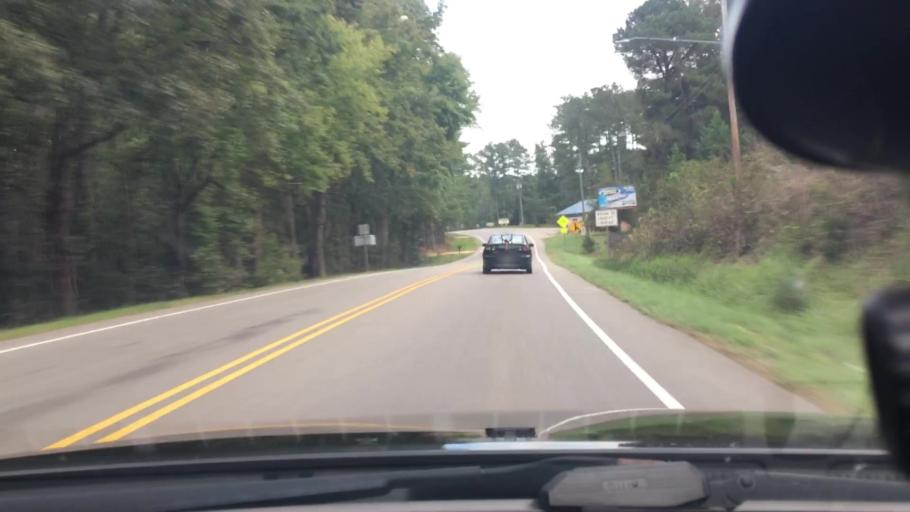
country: US
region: North Carolina
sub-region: Moore County
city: Carthage
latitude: 35.3583
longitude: -79.4335
